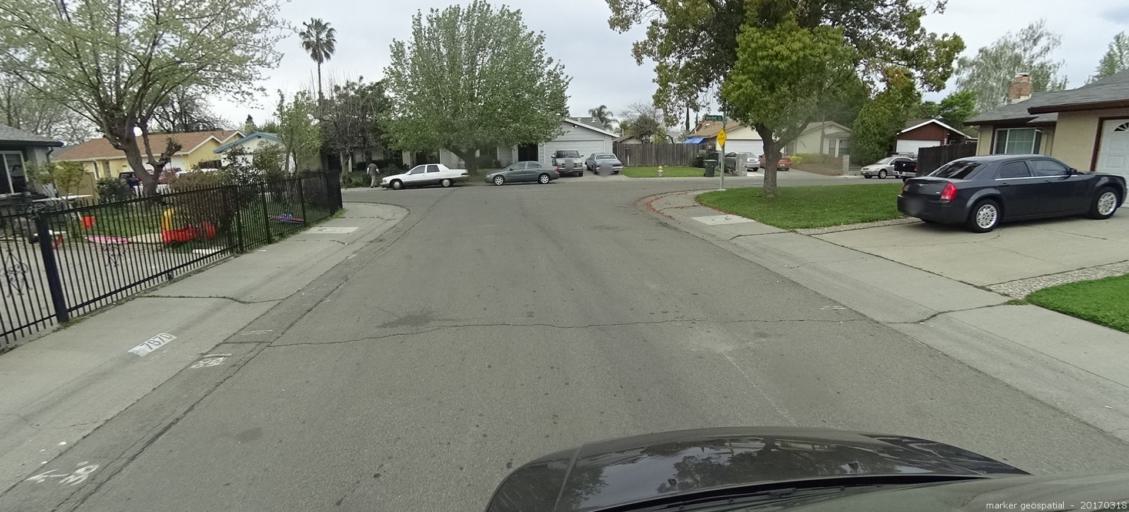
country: US
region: California
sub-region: Sacramento County
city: Florin
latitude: 38.4789
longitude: -121.4328
